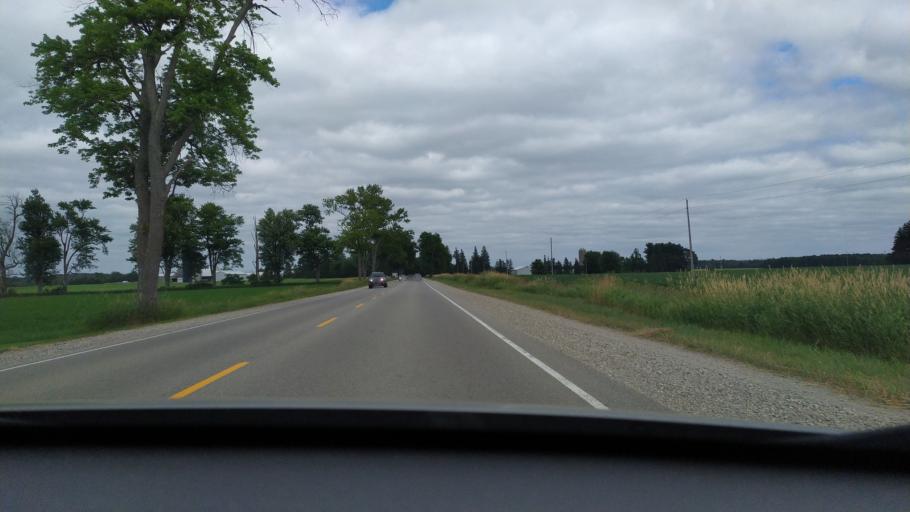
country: CA
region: Ontario
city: Stratford
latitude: 43.3160
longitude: -80.9705
